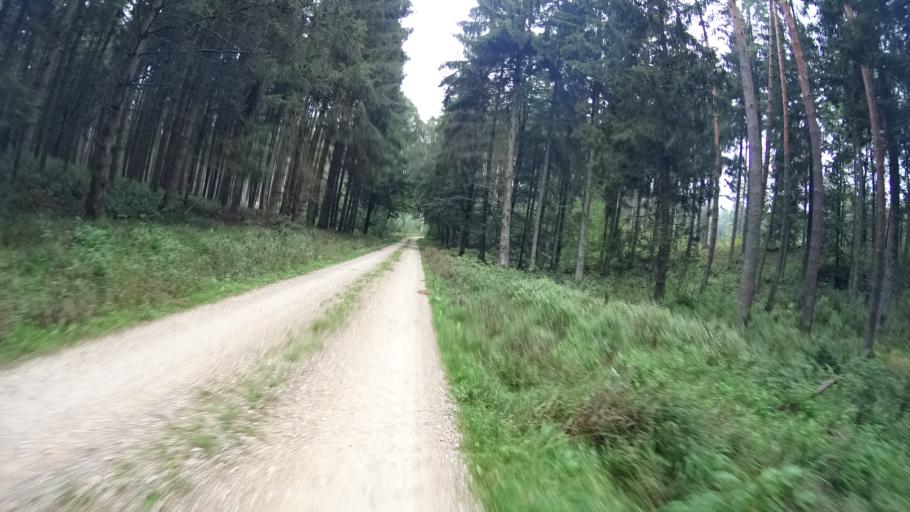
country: DE
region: Bavaria
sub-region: Upper Bavaria
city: Stammham
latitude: 48.8900
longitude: 11.5073
